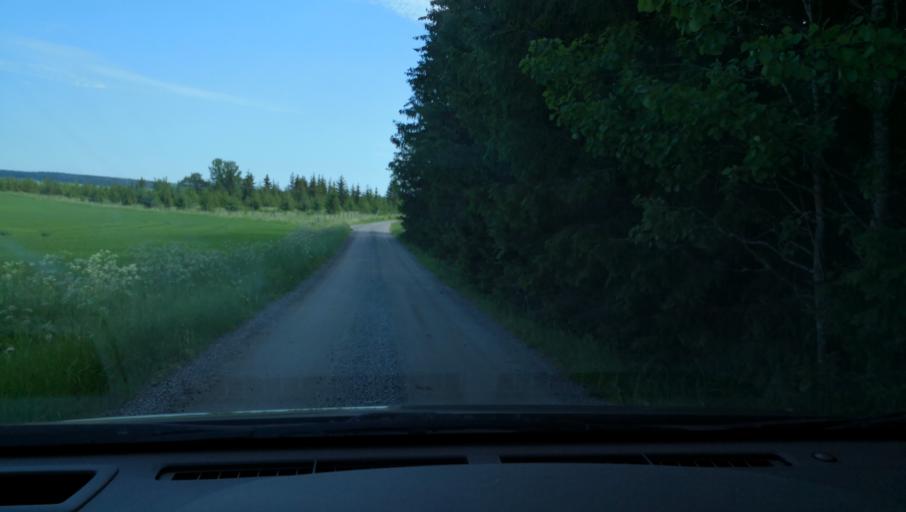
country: SE
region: Uppsala
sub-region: Enkopings Kommun
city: Enkoping
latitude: 59.7006
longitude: 17.1139
